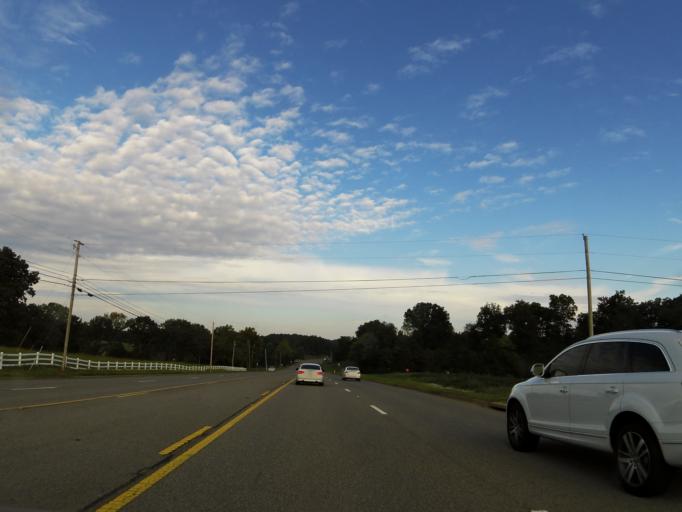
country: US
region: Alabama
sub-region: Lauderdale County
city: Rogersville
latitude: 34.8111
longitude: -87.2450
